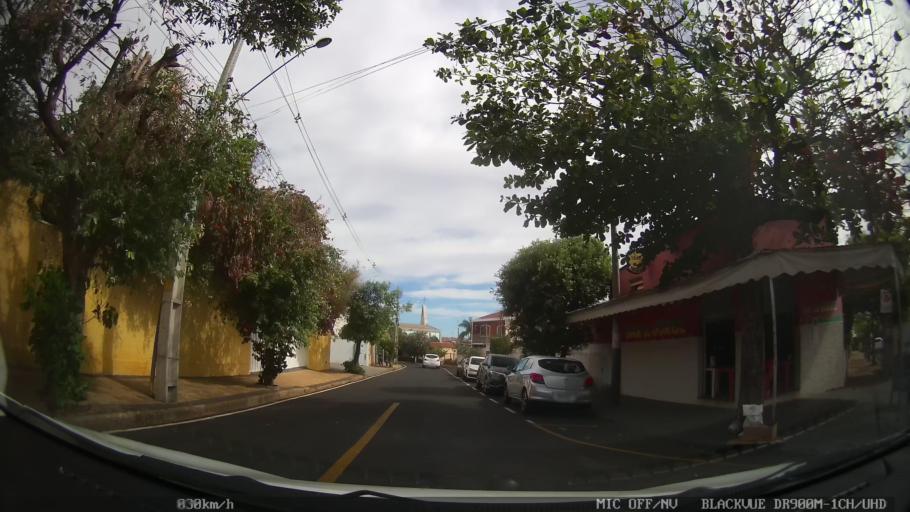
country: BR
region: Sao Paulo
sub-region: Catanduva
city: Catanduva
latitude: -21.1455
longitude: -48.9674
